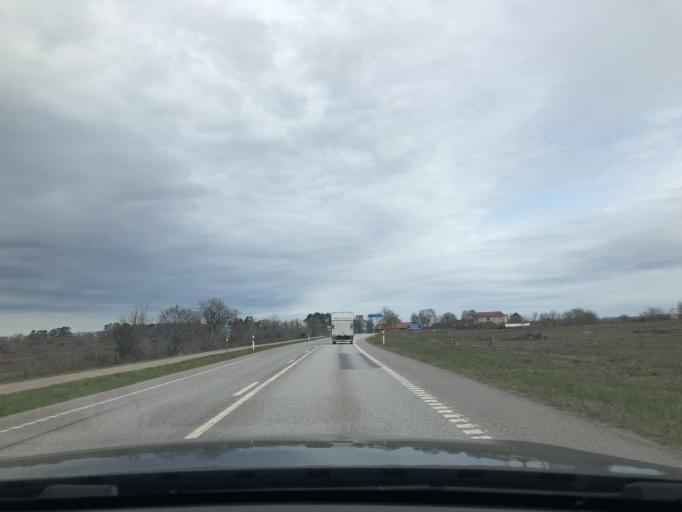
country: SE
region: Kalmar
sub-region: Borgholms Kommun
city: Borgholm
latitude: 56.8648
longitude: 16.6547
